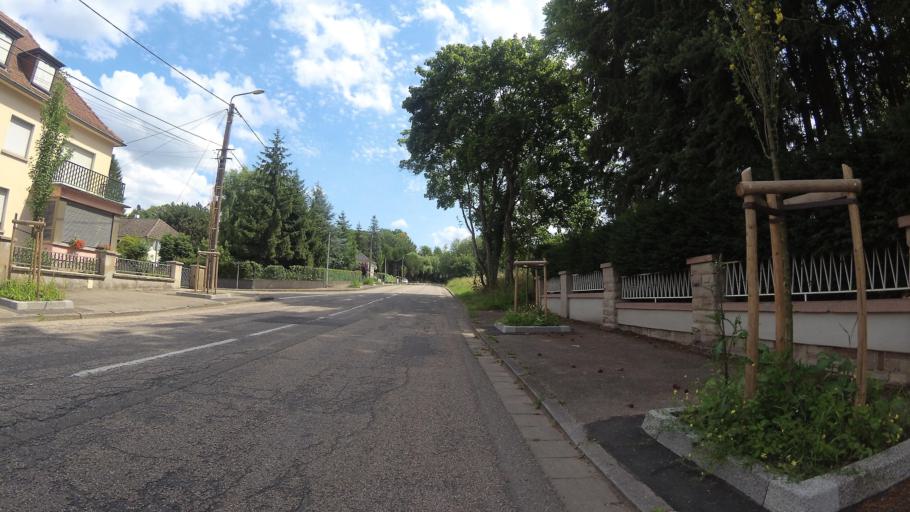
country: FR
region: Lorraine
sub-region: Departement de la Moselle
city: Sarreguemines
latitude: 49.1185
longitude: 7.0790
